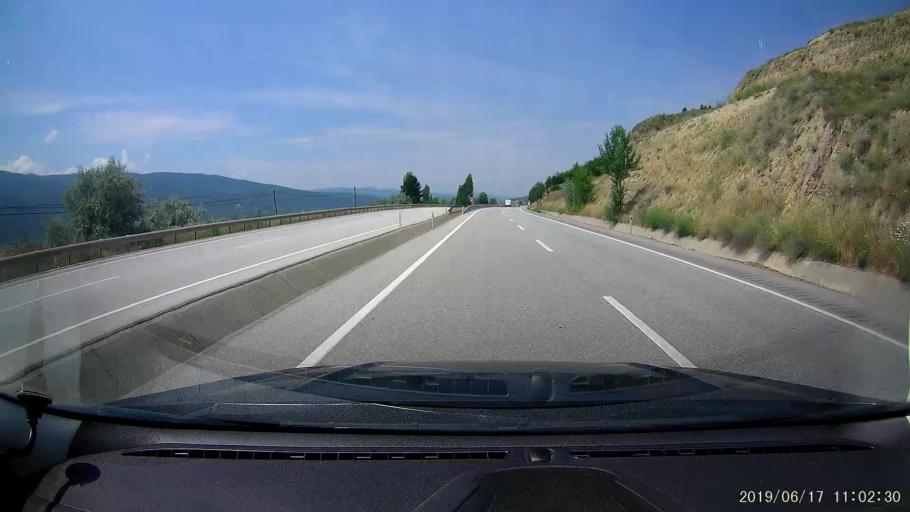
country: TR
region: Kastamonu
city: Tosya
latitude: 41.0174
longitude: 34.1350
